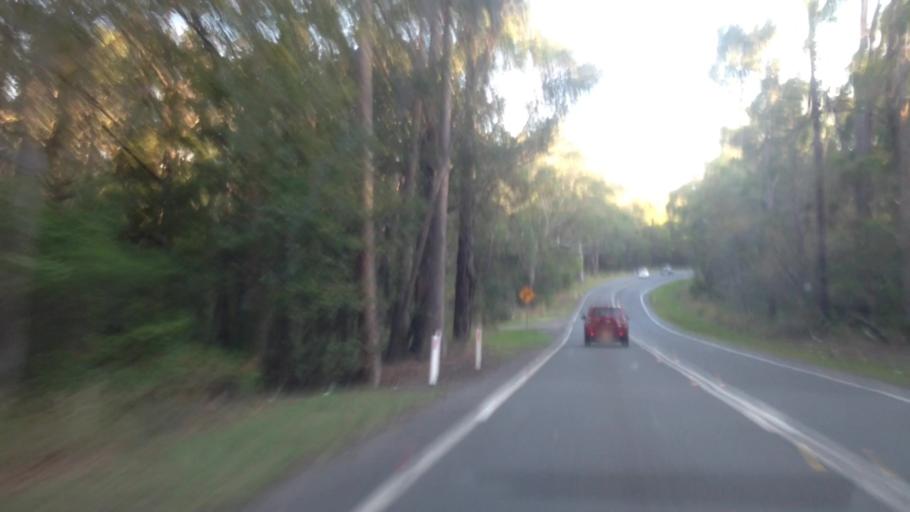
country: AU
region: New South Wales
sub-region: Lake Macquarie Shire
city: Dora Creek
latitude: -32.9992
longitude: 151.4924
